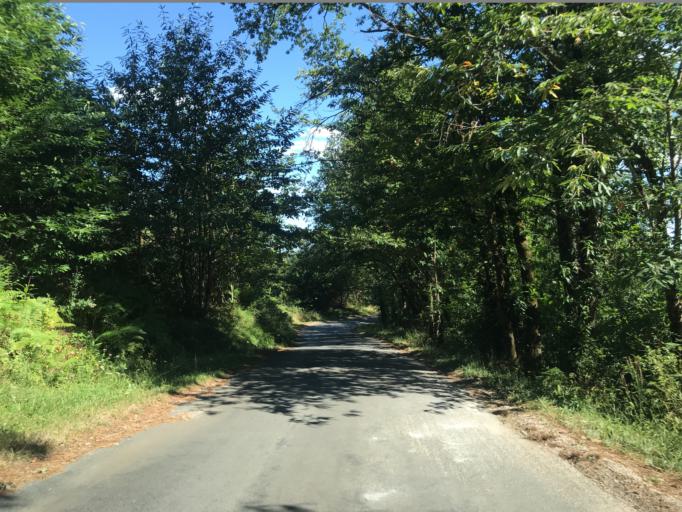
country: FR
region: Aquitaine
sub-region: Departement de la Dordogne
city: Sarlat-la-Caneda
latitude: 44.9223
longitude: 1.1971
